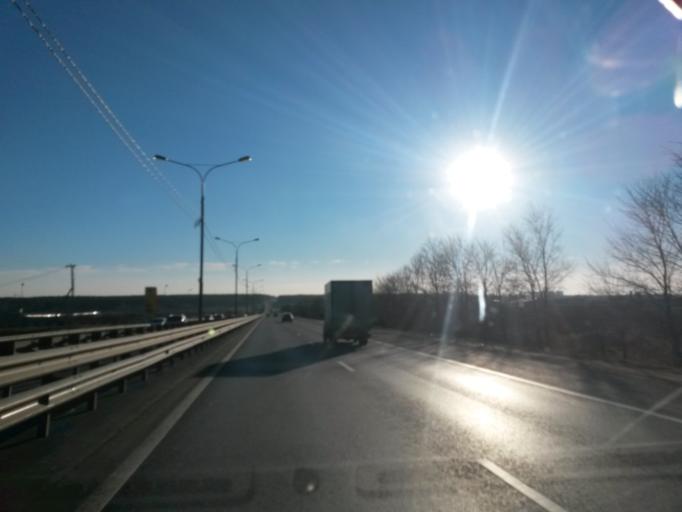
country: RU
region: Moskovskaya
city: Lesnoy
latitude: 56.0564
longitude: 37.8994
